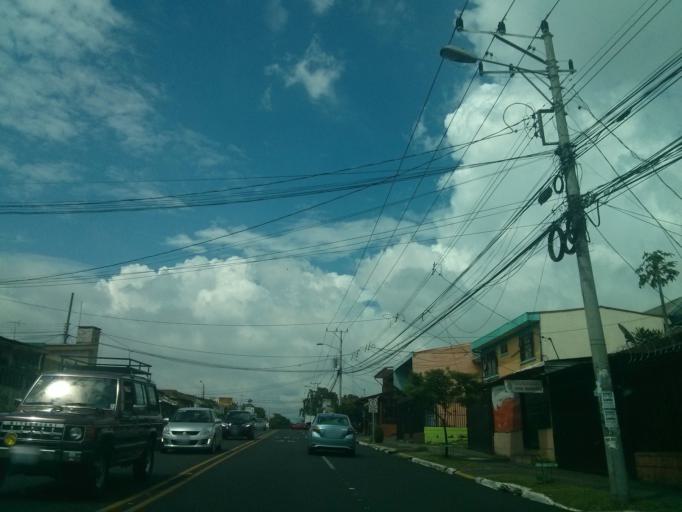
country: CR
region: San Jose
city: San Pedro
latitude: 9.9076
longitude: -84.0568
